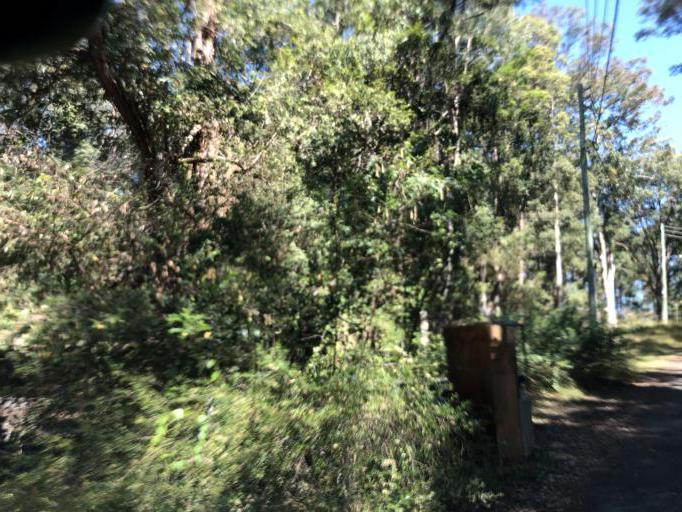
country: AU
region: New South Wales
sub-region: Bellingen
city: Bellingen
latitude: -30.4616
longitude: 152.8988
